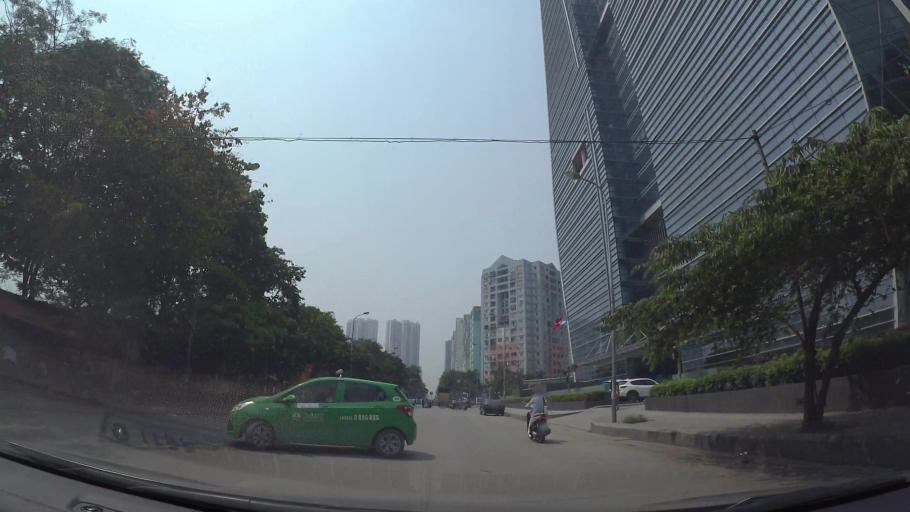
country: VN
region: Ha Noi
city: Thanh Xuan
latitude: 21.0014
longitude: 105.8011
